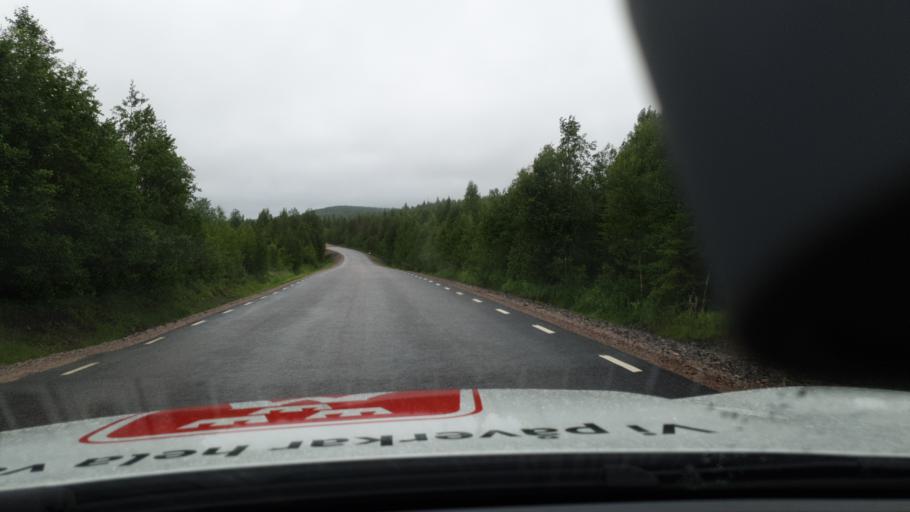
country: SE
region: Norrbotten
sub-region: Overtornea Kommun
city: OEvertornea
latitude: 66.5262
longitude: 23.3712
